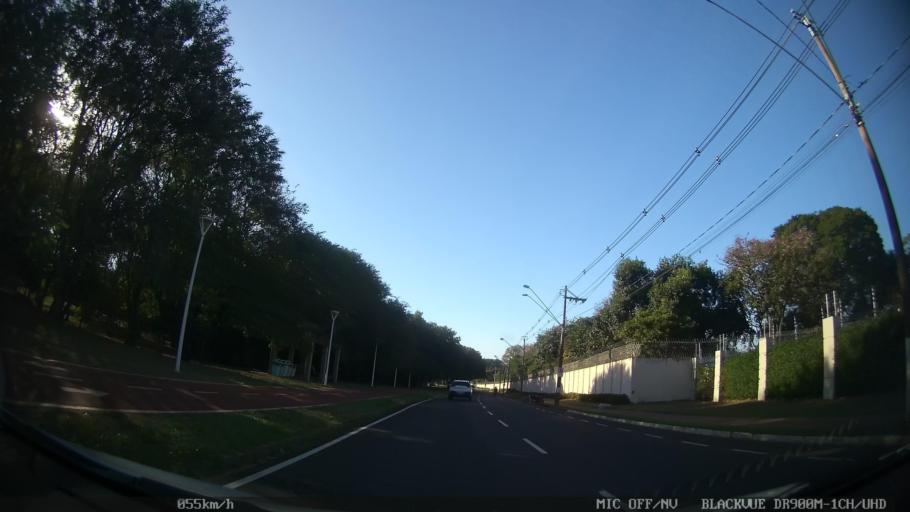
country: BR
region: Sao Paulo
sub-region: Sao Jose Do Rio Preto
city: Sao Jose do Rio Preto
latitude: -20.8477
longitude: -49.4120
